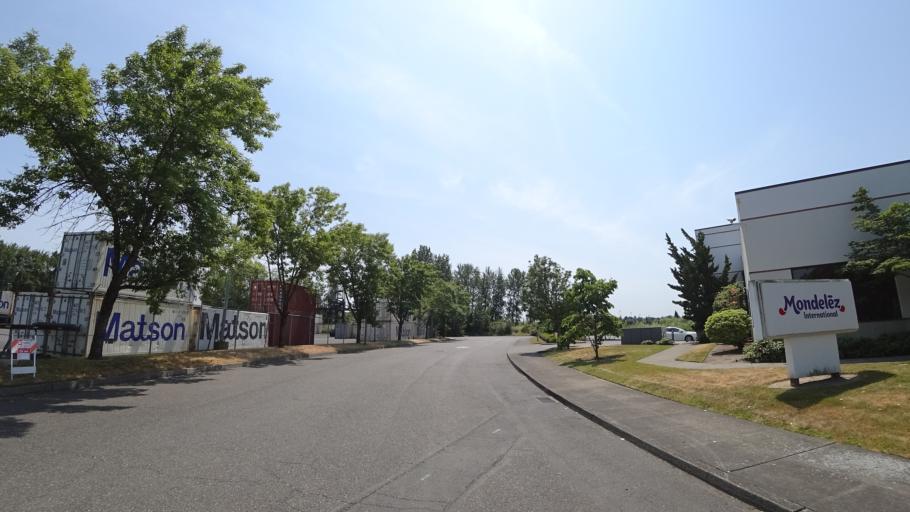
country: US
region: Washington
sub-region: Clark County
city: Vancouver
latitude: 45.5957
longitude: -122.6736
